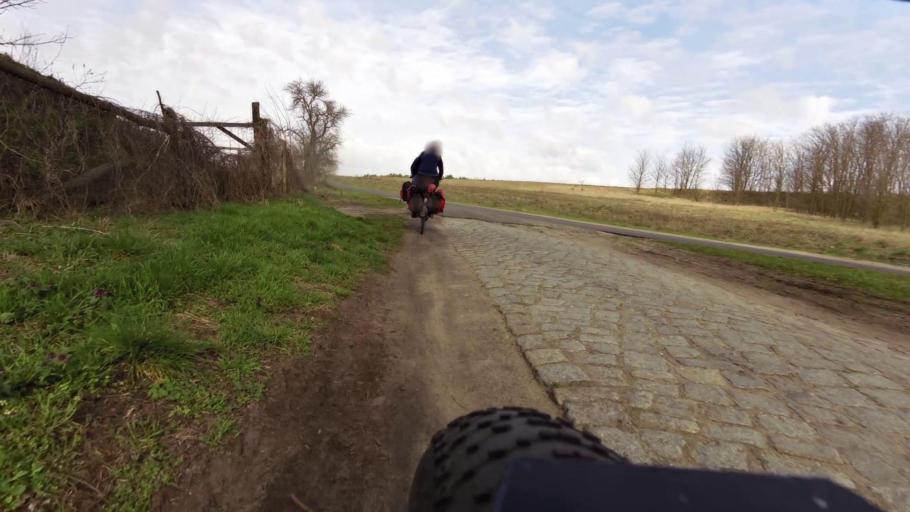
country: DE
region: Brandenburg
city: Brieskow-Finkenheerd
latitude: 52.2855
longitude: 14.6179
